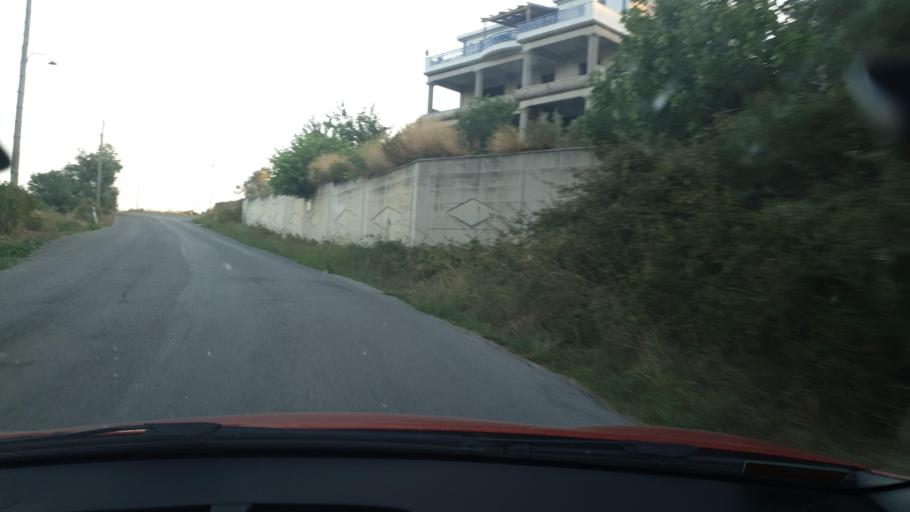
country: GR
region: Central Greece
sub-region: Nomos Evvoias
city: Oxilithos
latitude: 38.5703
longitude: 24.1212
